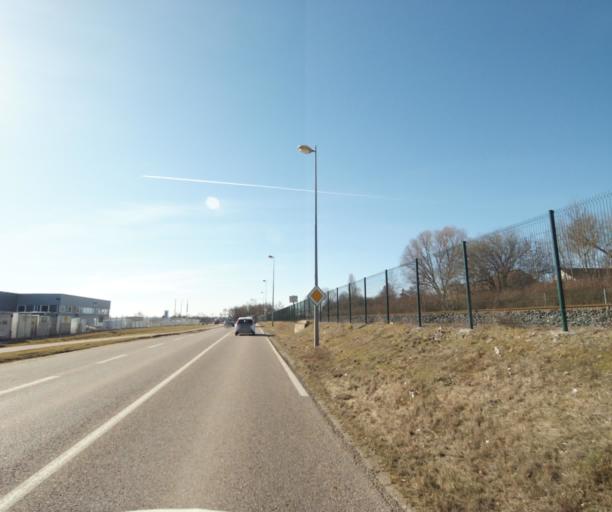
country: FR
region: Lorraine
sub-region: Departement de Meurthe-et-Moselle
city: Ludres
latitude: 48.6268
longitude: 6.1793
